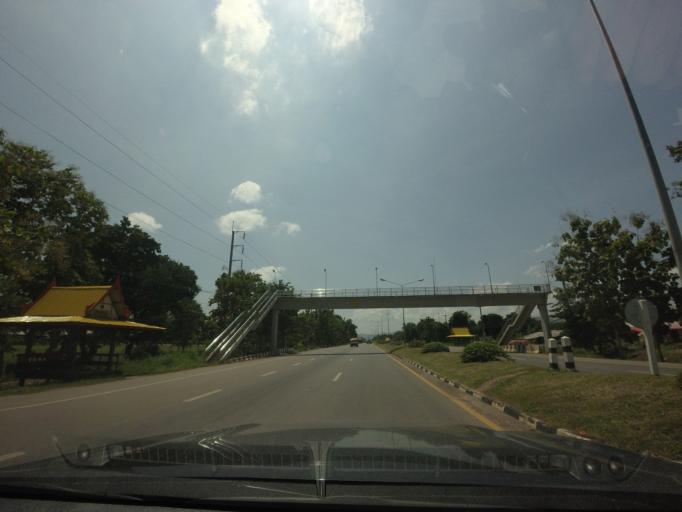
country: TH
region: Phetchabun
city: Lom Sak
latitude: 16.7012
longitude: 101.1729
